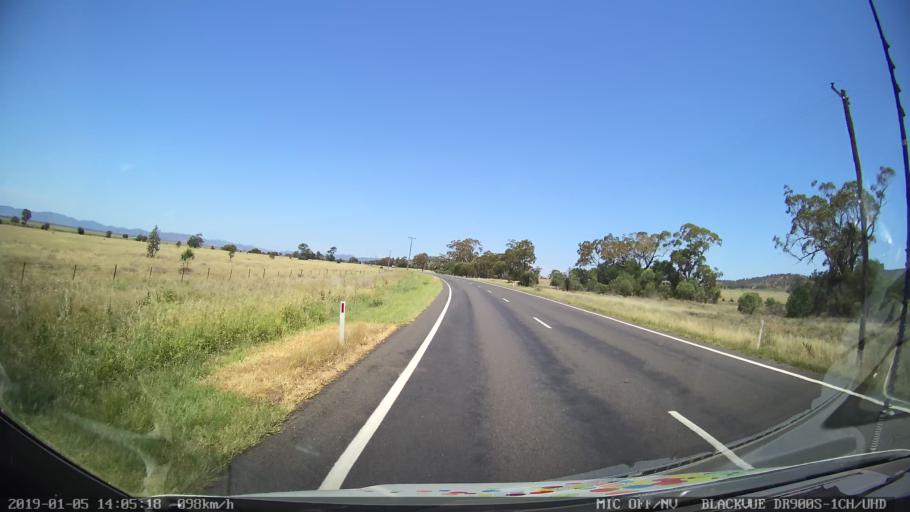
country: AU
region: New South Wales
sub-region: Gunnedah
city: Gunnedah
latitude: -31.2096
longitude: 150.3733
